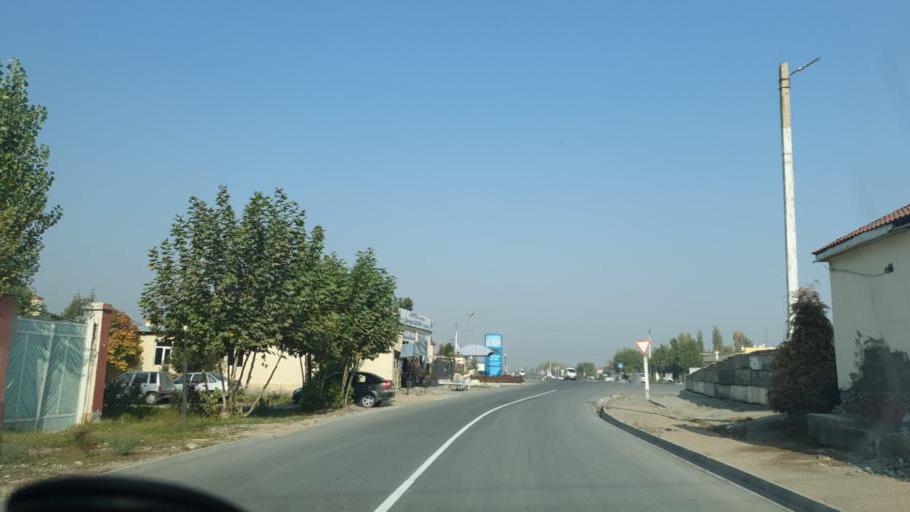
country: UZ
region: Fergana
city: Qo`qon
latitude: 40.5874
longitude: 70.9051
